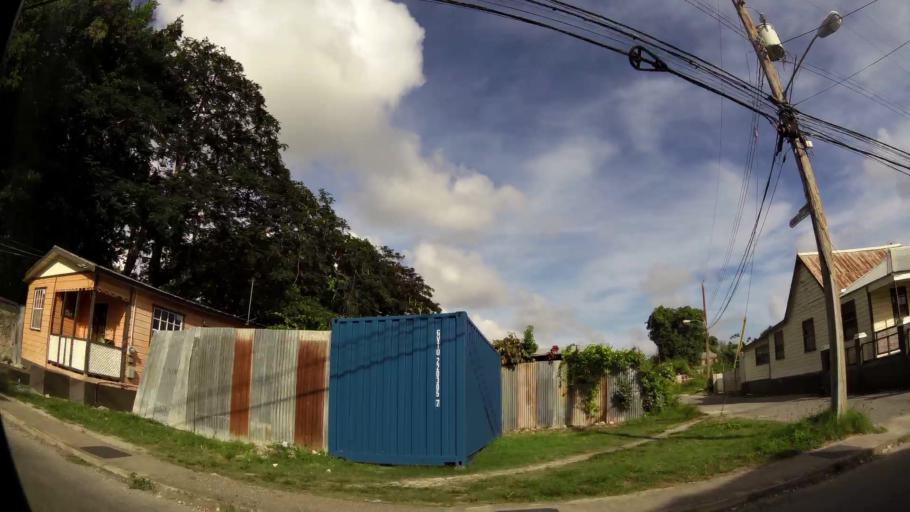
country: BB
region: Saint Michael
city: Bridgetown
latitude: 13.0811
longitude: -59.6015
